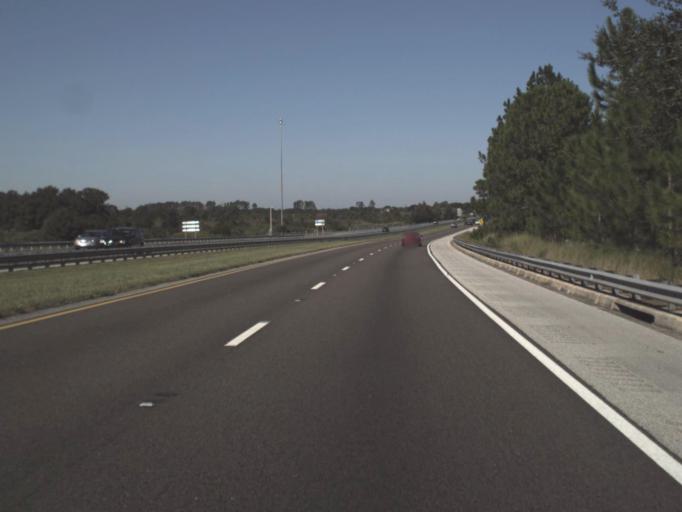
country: US
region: Florida
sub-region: Lake County
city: Yalaha
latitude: 28.6770
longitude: -81.8557
